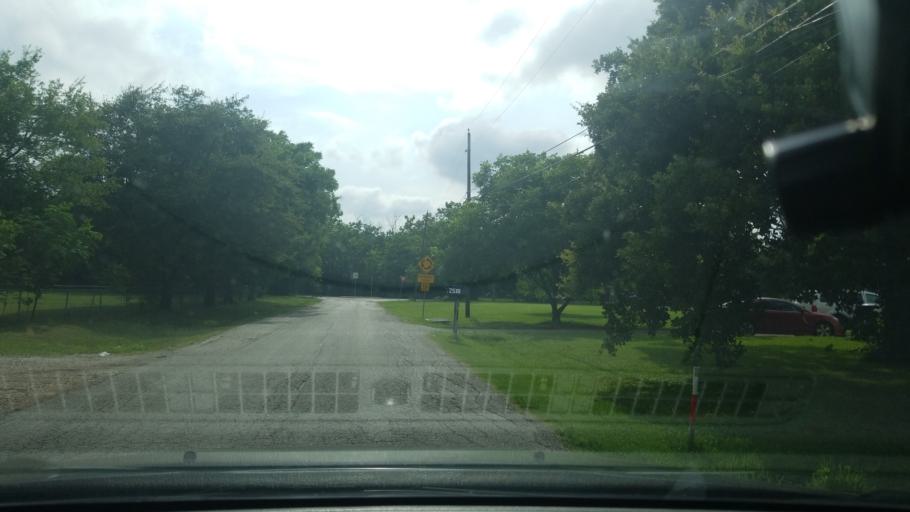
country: US
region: Texas
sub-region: Dallas County
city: Balch Springs
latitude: 32.7576
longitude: -96.6377
